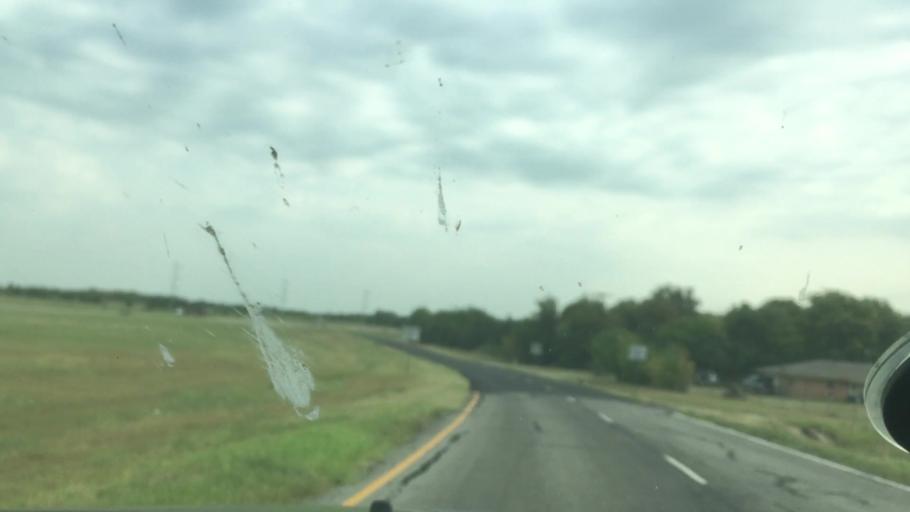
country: US
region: Texas
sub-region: Grayson County
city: Denison
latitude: 33.7785
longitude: -96.5826
